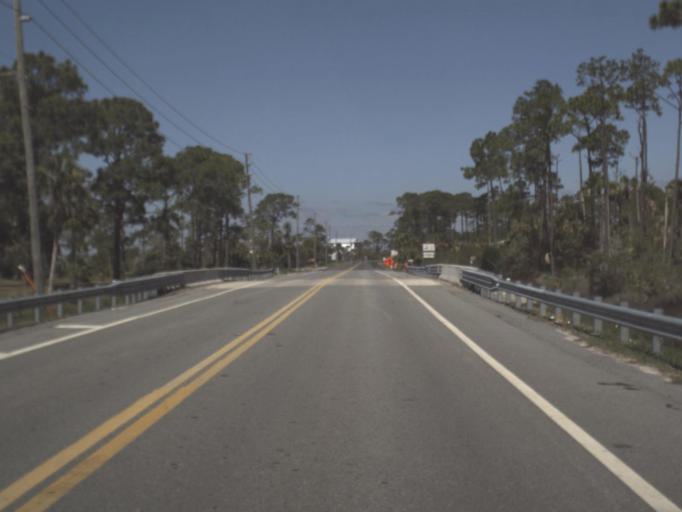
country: US
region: Florida
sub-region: Gulf County
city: Port Saint Joe
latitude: 29.7475
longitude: -85.3028
